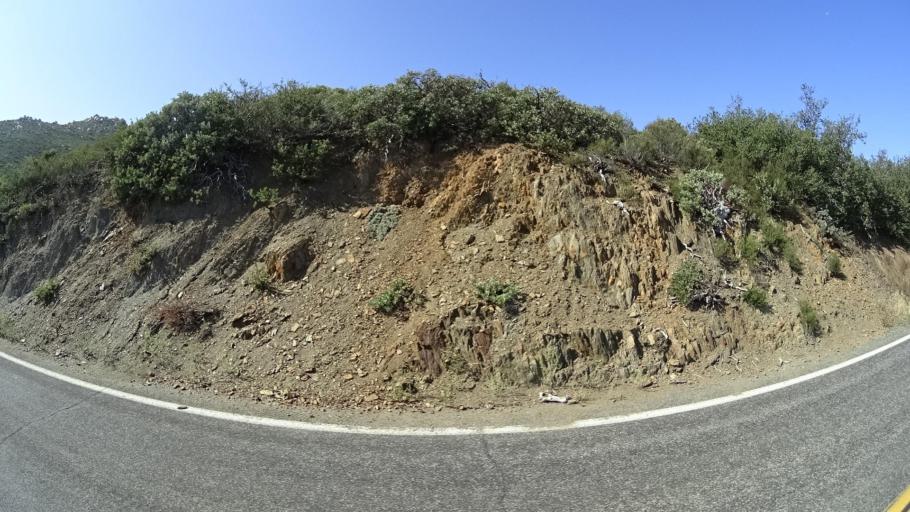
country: US
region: California
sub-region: San Diego County
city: Julian
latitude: 32.9759
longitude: -116.5206
